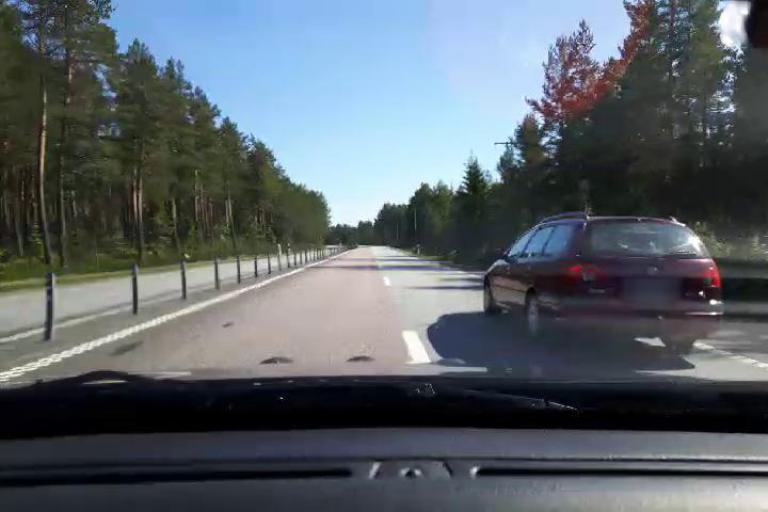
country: SE
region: Gaevleborg
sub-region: Gavle Kommun
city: Norrsundet
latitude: 61.0218
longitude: 16.9765
